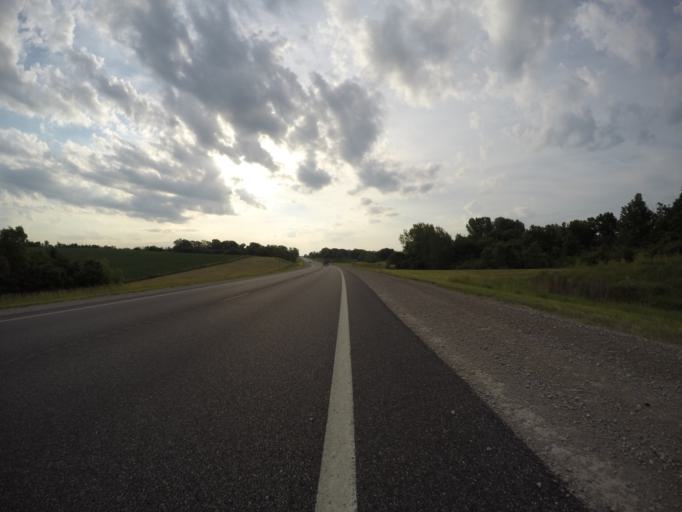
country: US
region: Kansas
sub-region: Doniphan County
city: Troy
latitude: 39.7925
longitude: -95.0736
